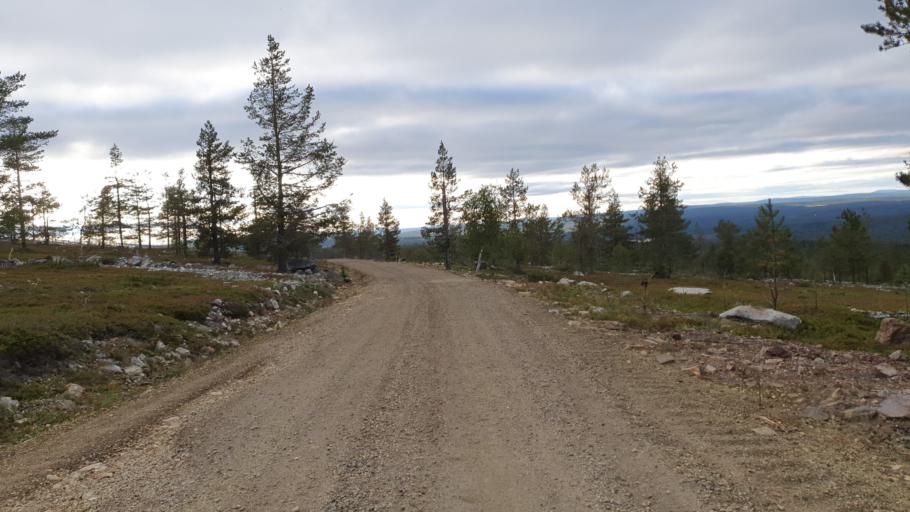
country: FI
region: Lapland
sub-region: Tunturi-Lappi
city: Kolari
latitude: 67.5791
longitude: 24.2228
